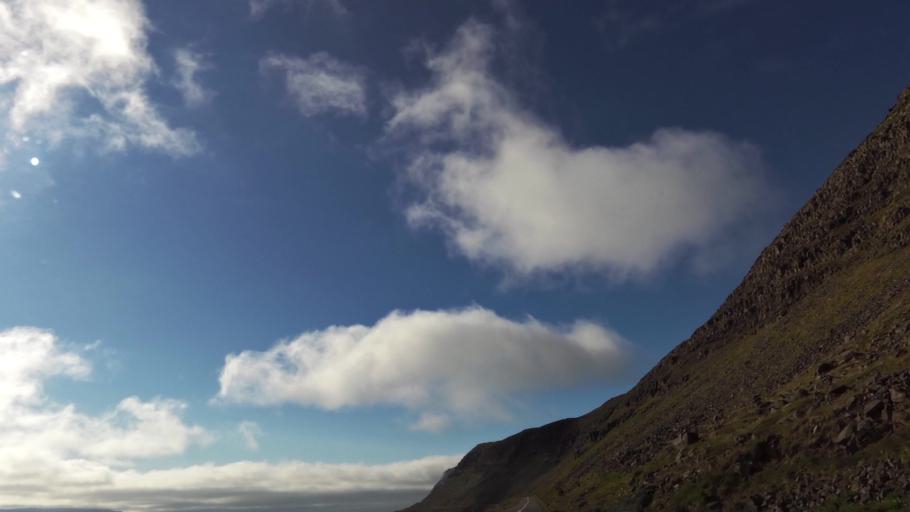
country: IS
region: West
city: Olafsvik
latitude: 65.5730
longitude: -23.9389
